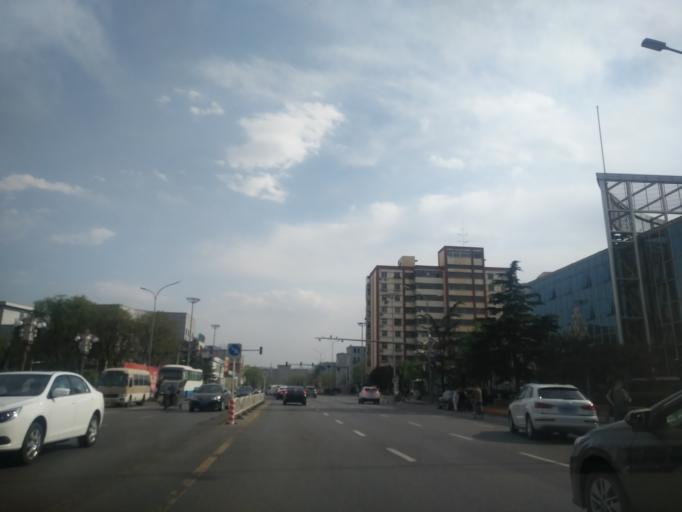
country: CN
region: Beijing
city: Xingfeng
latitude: 39.7265
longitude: 116.3335
